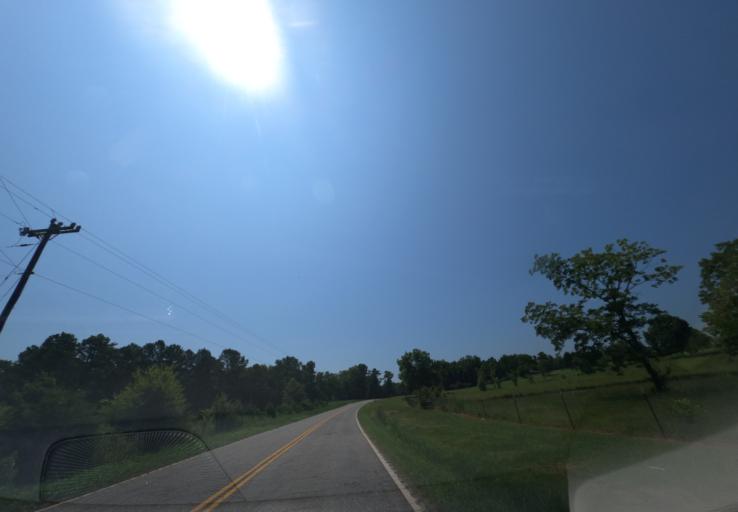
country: US
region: South Carolina
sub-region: Greenwood County
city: Greenwood
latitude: 34.0569
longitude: -82.1376
